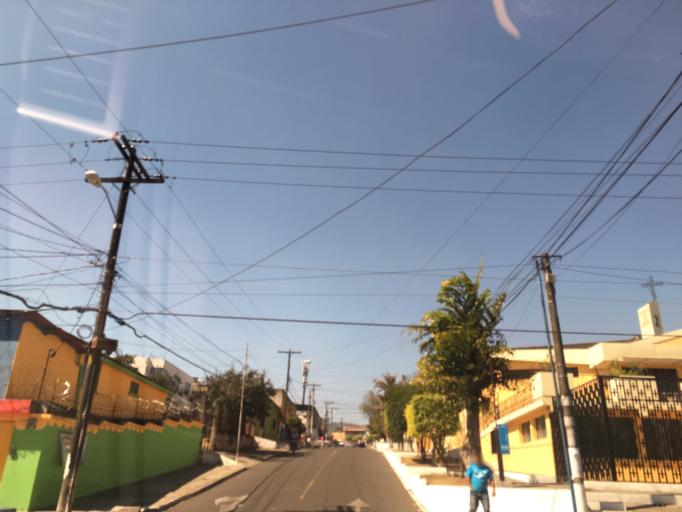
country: GT
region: Guatemala
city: Mixco
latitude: 14.6309
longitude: -90.5824
